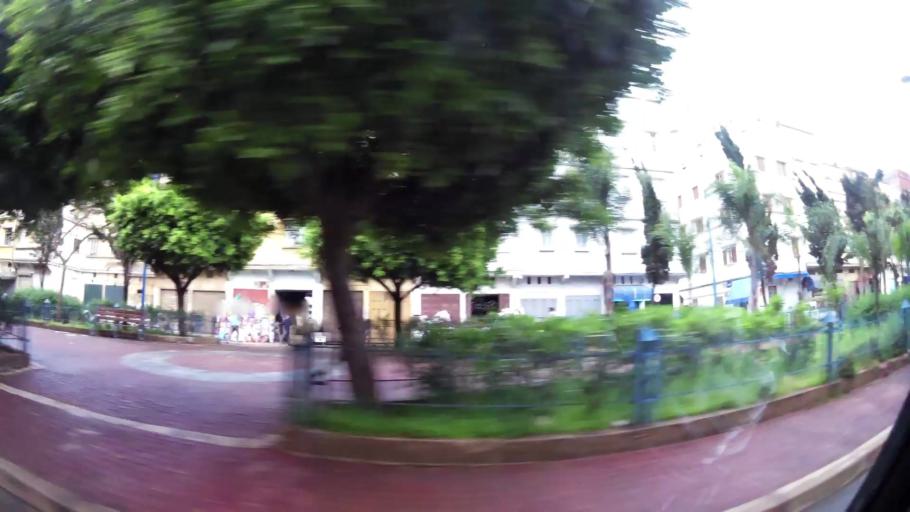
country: MA
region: Grand Casablanca
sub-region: Casablanca
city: Casablanca
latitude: 33.5545
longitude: -7.5800
